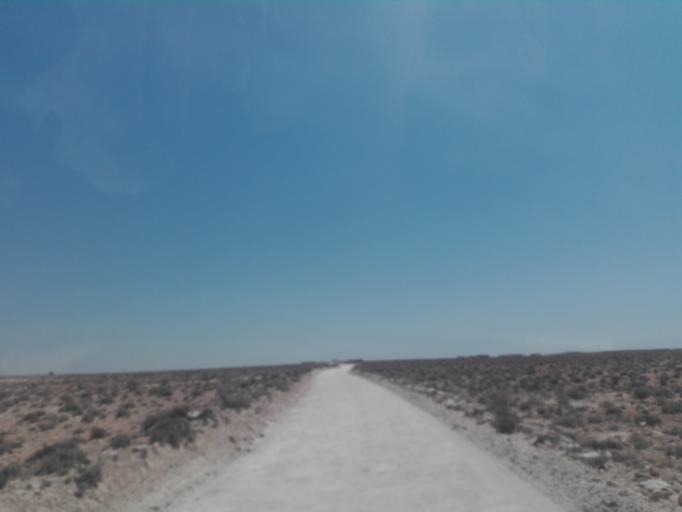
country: TN
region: Safaqis
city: Skhira
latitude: 34.4183
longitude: 9.9547
